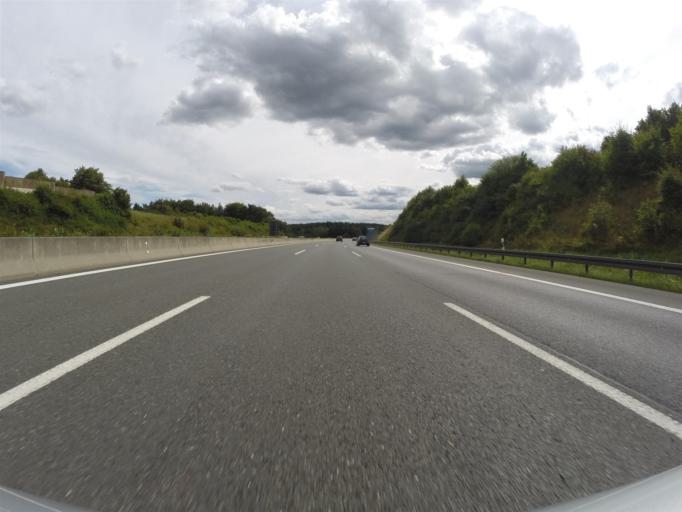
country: DE
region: Bavaria
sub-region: Upper Franconia
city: Pegnitz
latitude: 49.7364
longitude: 11.5152
